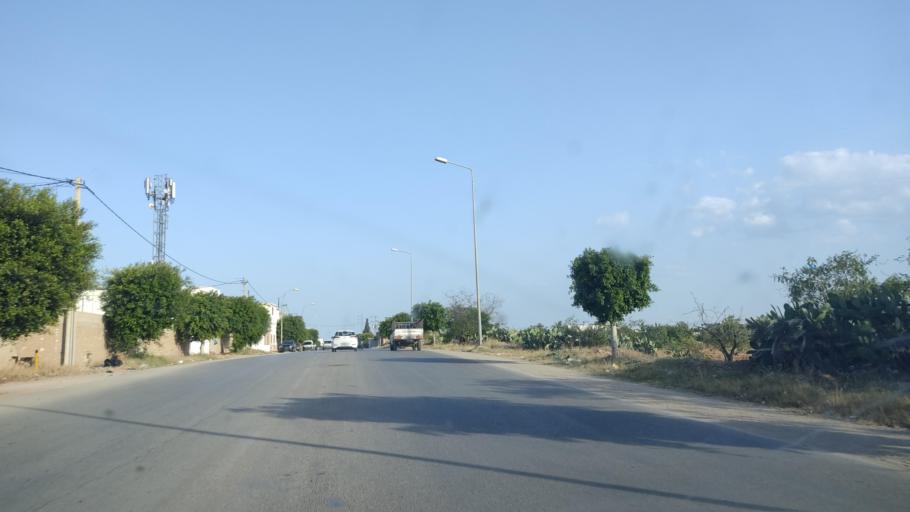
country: TN
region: Safaqis
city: Sfax
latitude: 34.7897
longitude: 10.6882
